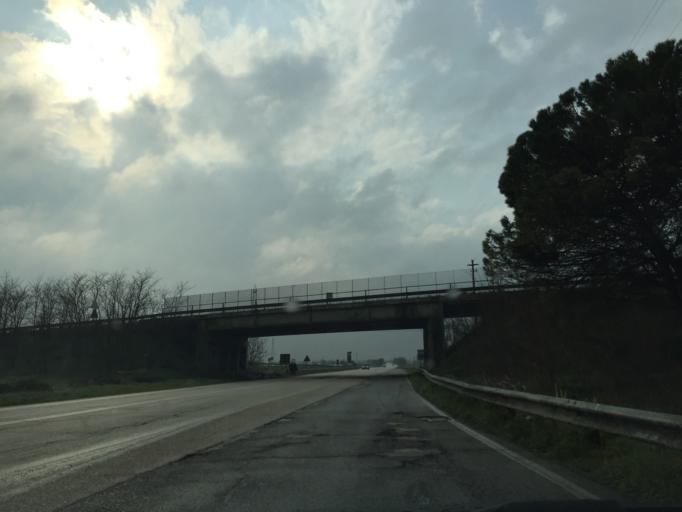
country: IT
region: Apulia
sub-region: Provincia di Foggia
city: Foggia
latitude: 41.4984
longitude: 15.5188
